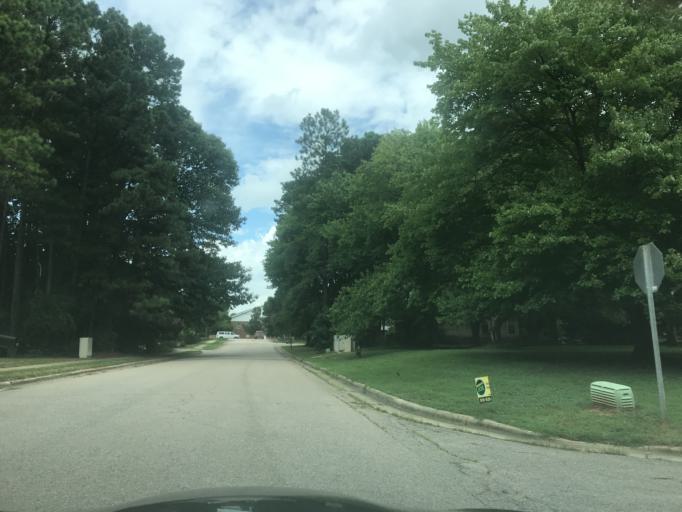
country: US
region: North Carolina
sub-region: Wake County
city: West Raleigh
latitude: 35.8944
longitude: -78.6127
